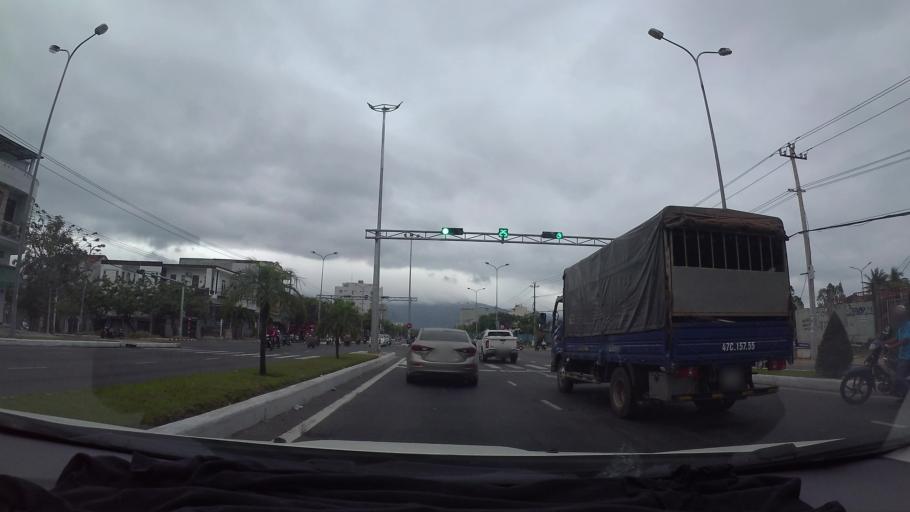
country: VN
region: Da Nang
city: Da Nang
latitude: 16.0836
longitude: 108.2377
